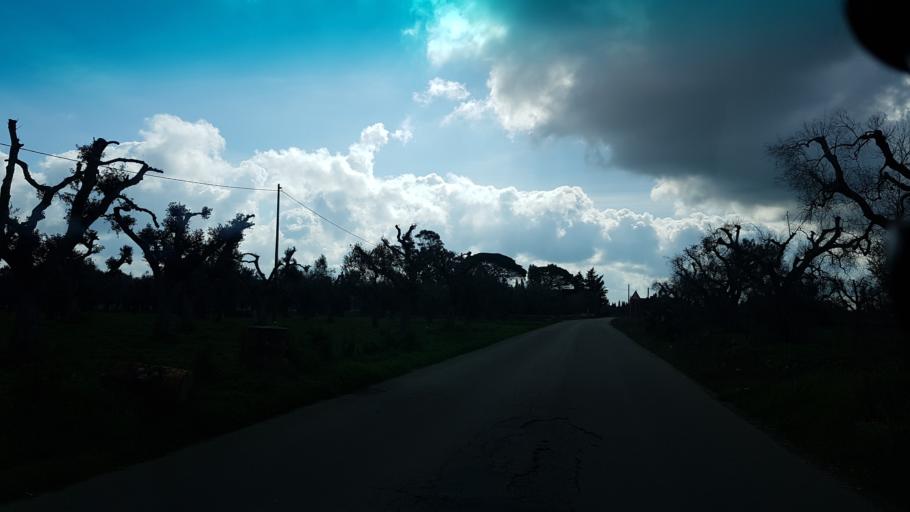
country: IT
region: Apulia
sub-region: Provincia di Lecce
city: Squinzano
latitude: 40.4480
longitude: 18.0417
